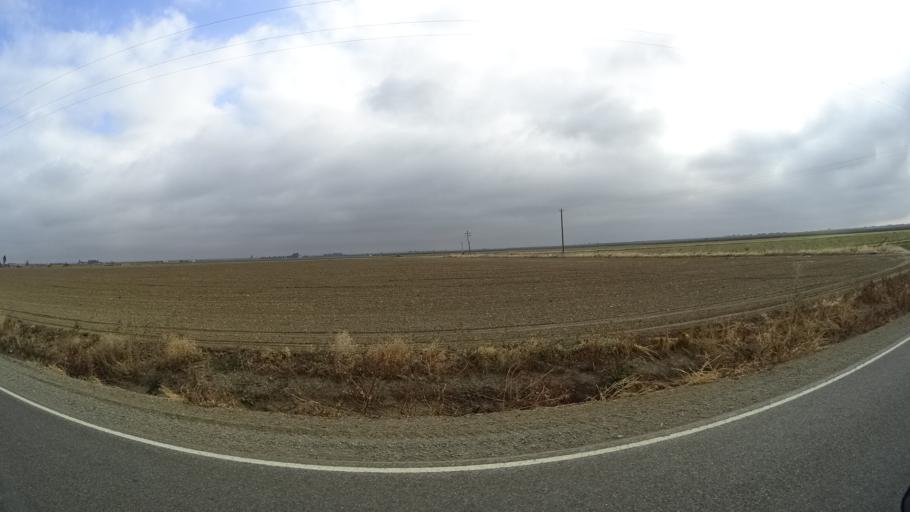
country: US
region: California
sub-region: Yolo County
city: Esparto
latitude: 38.7377
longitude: -122.0450
